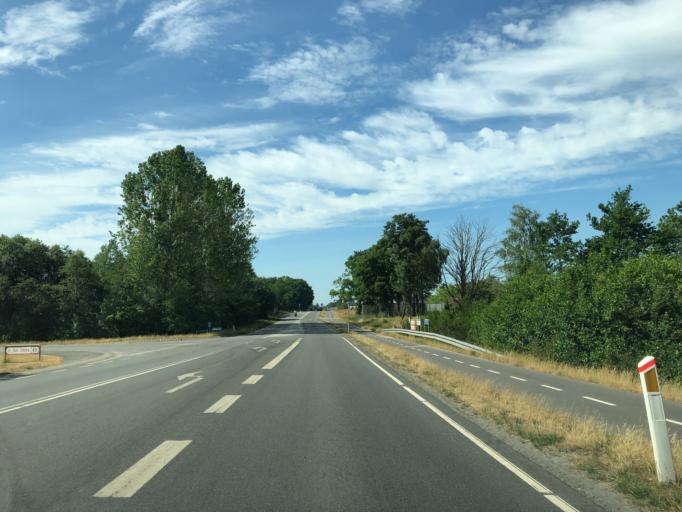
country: DK
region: Central Jutland
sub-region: Ikast-Brande Kommune
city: Brande
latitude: 55.9572
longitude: 9.1082
